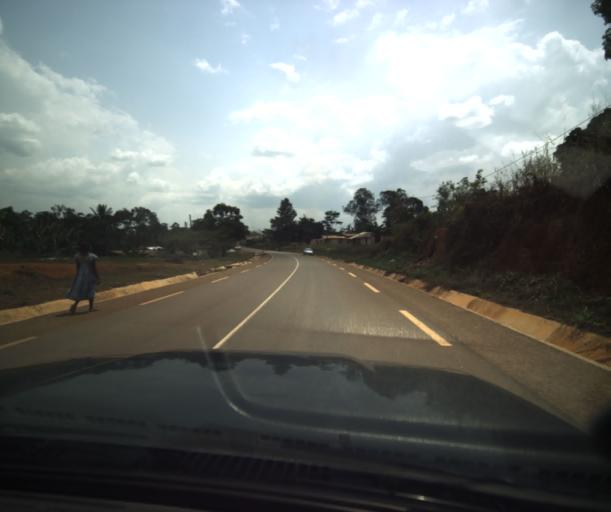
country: CM
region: Centre
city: Akono
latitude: 3.6048
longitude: 11.3100
